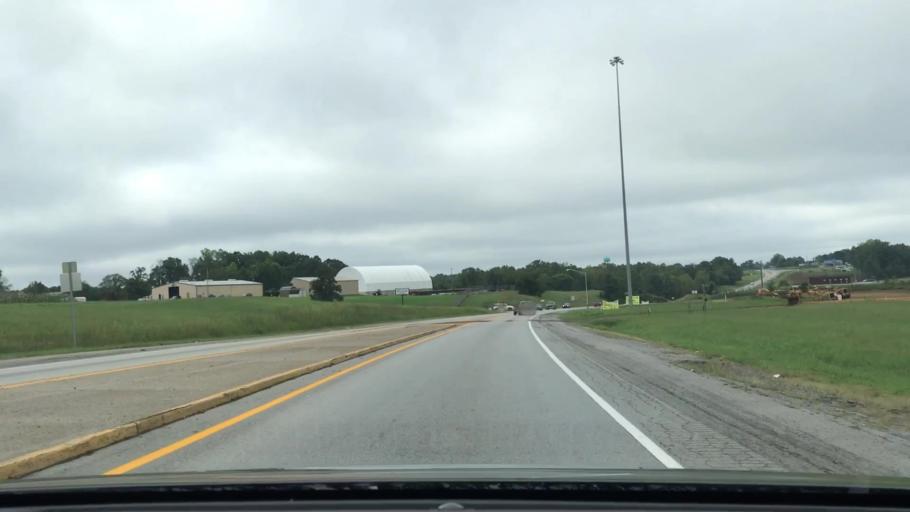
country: US
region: Kentucky
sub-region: Russell County
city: Russell Springs
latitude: 37.0478
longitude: -85.0701
